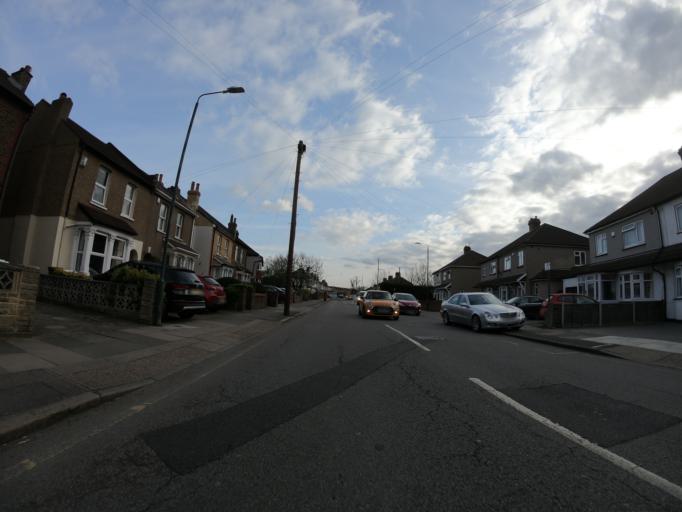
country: GB
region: England
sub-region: Greater London
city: Bexleyheath
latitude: 51.4645
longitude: 0.1402
